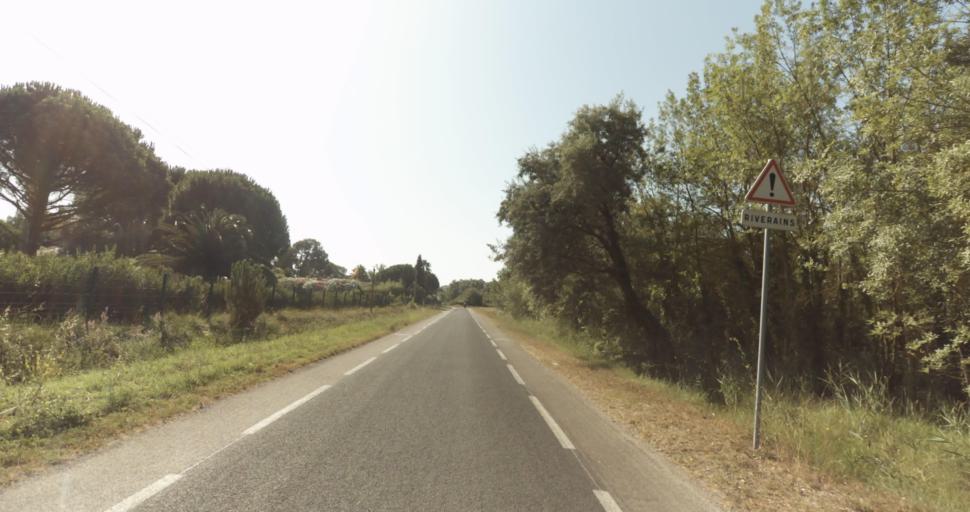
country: FR
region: Languedoc-Roussillon
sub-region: Departement des Pyrenees-Orientales
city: Saint-Cyprien-Plage
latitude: 42.6309
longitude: 3.0117
